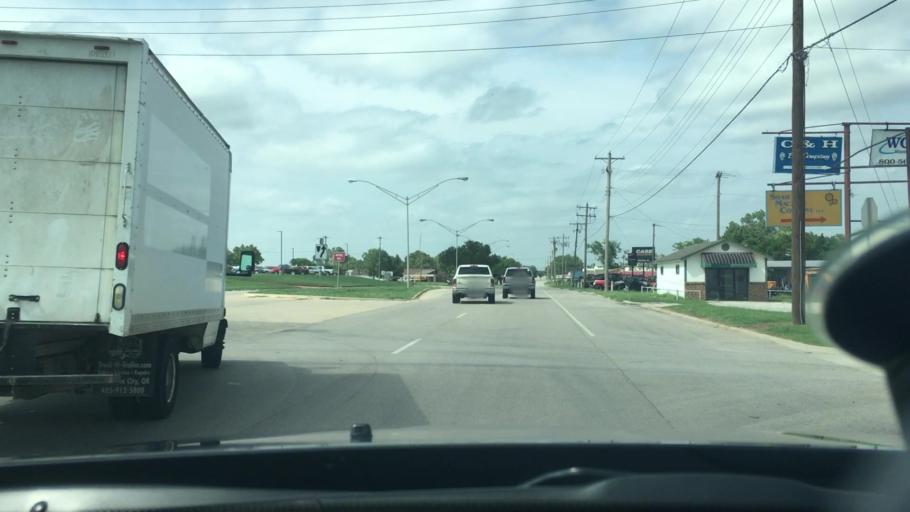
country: US
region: Oklahoma
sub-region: Pontotoc County
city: Ada
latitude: 34.7943
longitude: -96.6786
